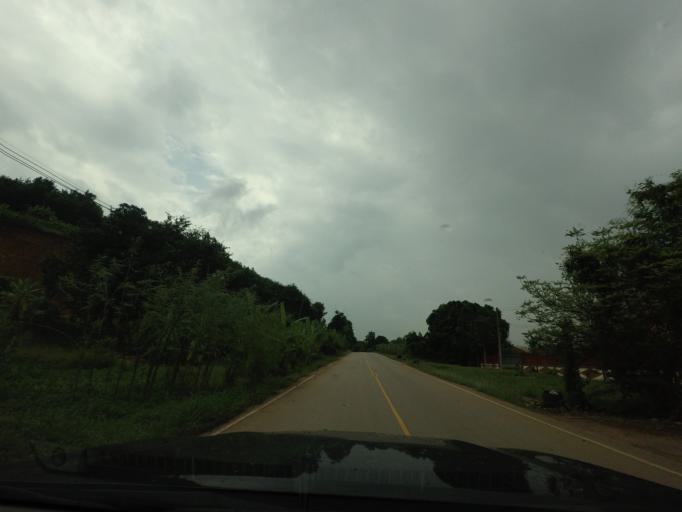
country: TH
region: Loei
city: Pak Chom
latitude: 18.1292
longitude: 102.0075
